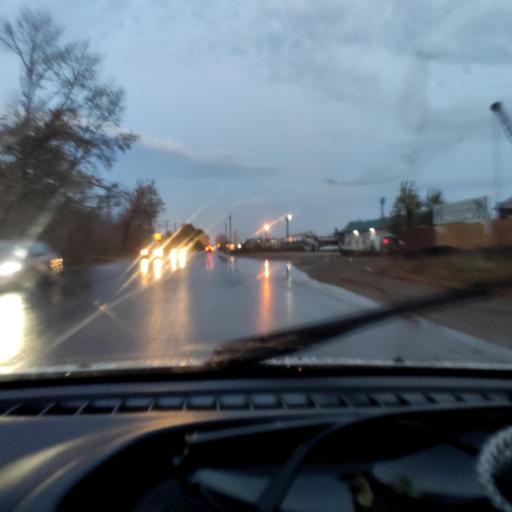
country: RU
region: Samara
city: Tol'yatti
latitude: 53.5311
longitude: 49.4617
